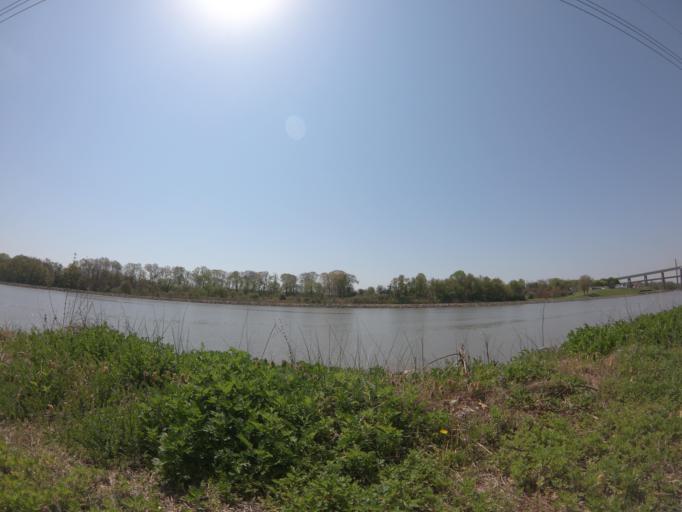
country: US
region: Delaware
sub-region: New Castle County
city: Delaware City
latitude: 39.5559
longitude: -75.6439
